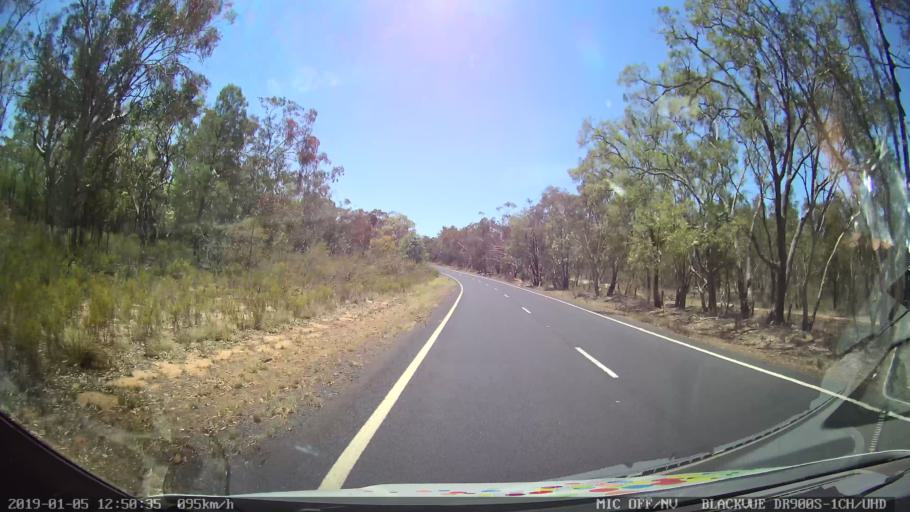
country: AU
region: New South Wales
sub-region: Warrumbungle Shire
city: Coonabarabran
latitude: -31.1203
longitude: 149.6257
